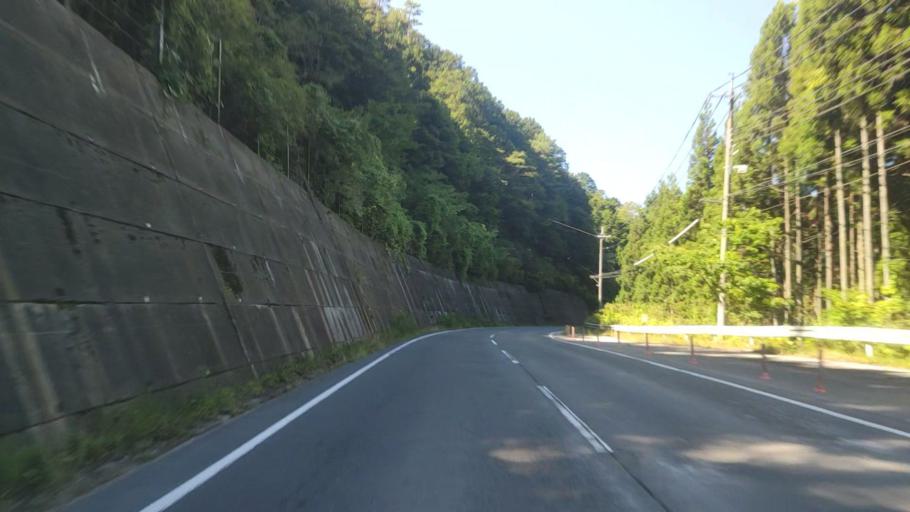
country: JP
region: Nara
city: Yoshino-cho
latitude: 34.4325
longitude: 135.9382
